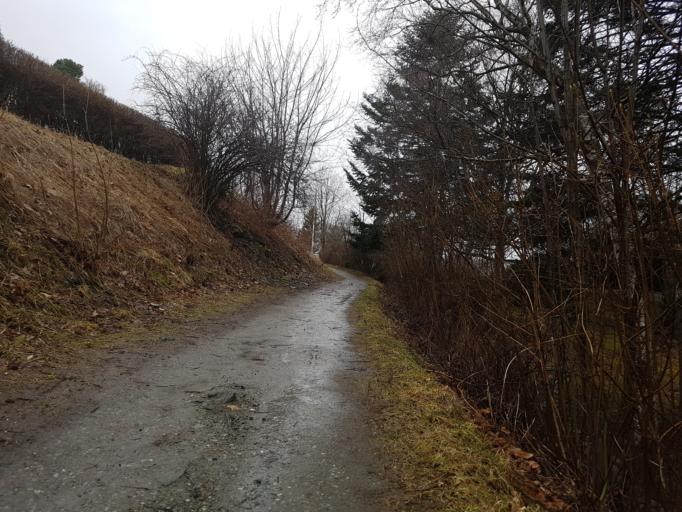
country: NO
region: Sor-Trondelag
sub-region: Trondheim
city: Trondheim
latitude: 63.4371
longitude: 10.4948
